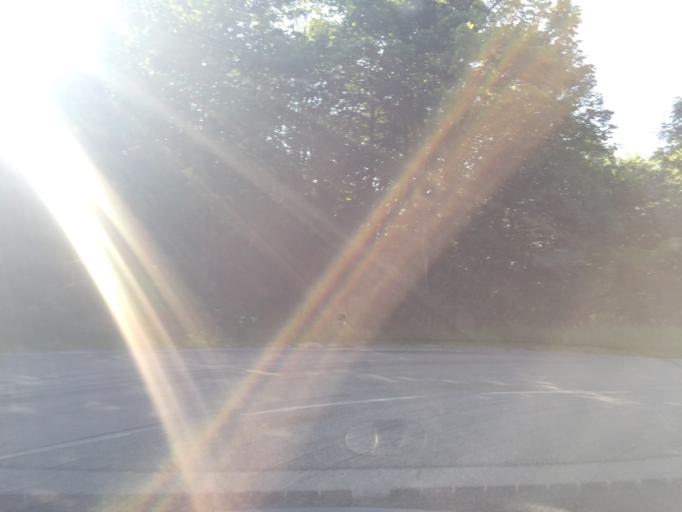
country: FR
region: Rhone-Alpes
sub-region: Departement de la Drome
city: Saint-Laurent-en-Royans
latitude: 45.0312
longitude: 5.3474
